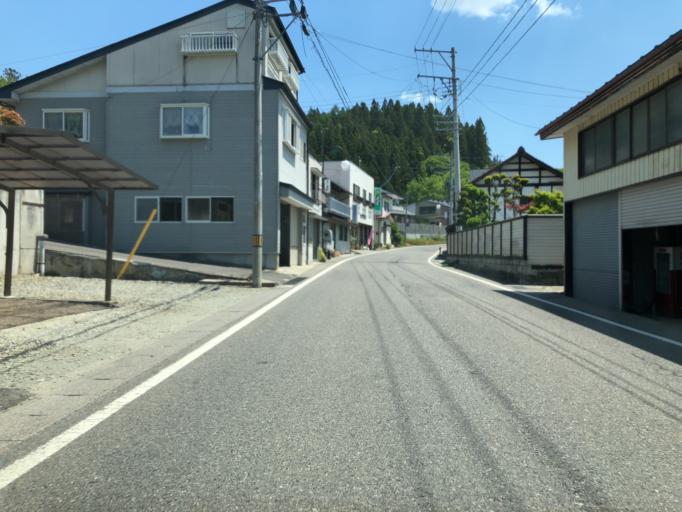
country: JP
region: Fukushima
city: Funehikimachi-funehiki
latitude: 37.5141
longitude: 140.6600
